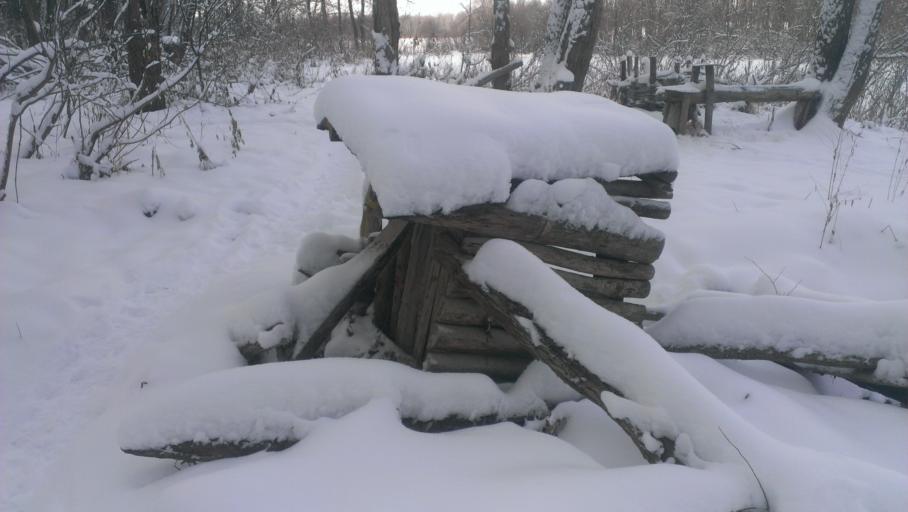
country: RU
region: Altai Krai
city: Nauchnyy Gorodok
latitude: 53.4257
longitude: 83.5017
